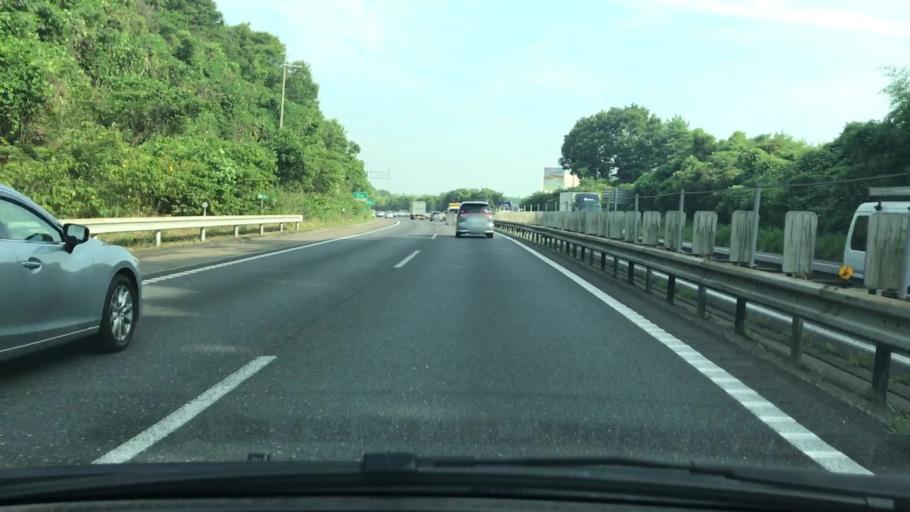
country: JP
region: Hyogo
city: Akashi
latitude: 34.6964
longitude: 134.9680
